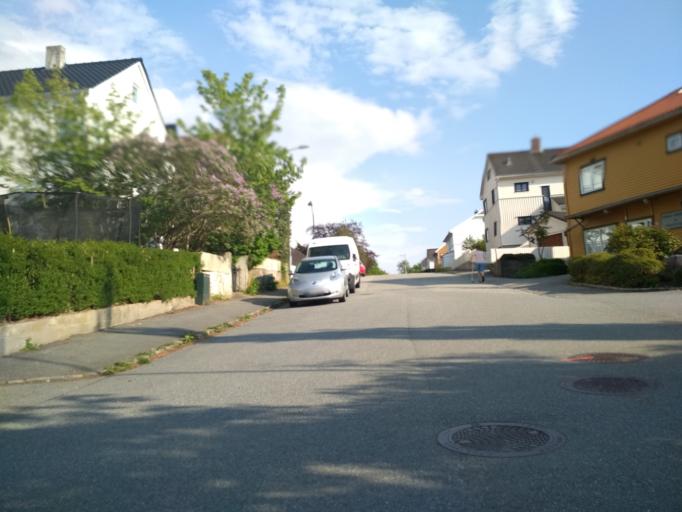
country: NO
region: Rogaland
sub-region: Stavanger
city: Stavanger
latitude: 58.9679
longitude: 5.7125
